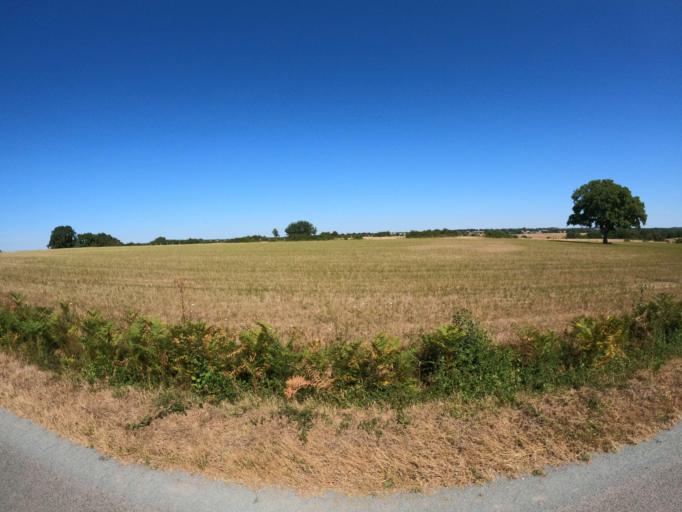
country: FR
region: Pays de la Loire
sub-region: Departement de Maine-et-Loire
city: Saint-Christophe-du-Bois
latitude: 47.0432
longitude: -0.9552
